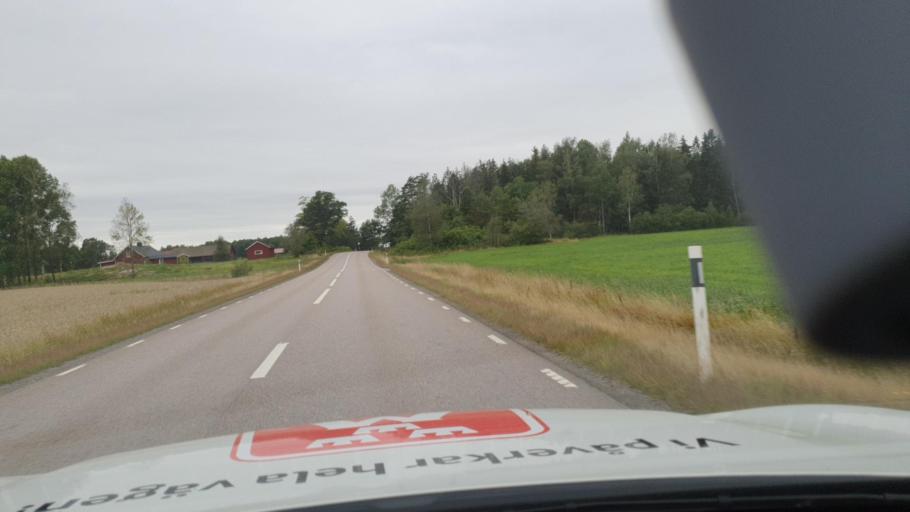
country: SE
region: Vaestra Goetaland
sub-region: Vanersborgs Kommun
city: Vanersborg
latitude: 58.4939
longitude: 12.2438
